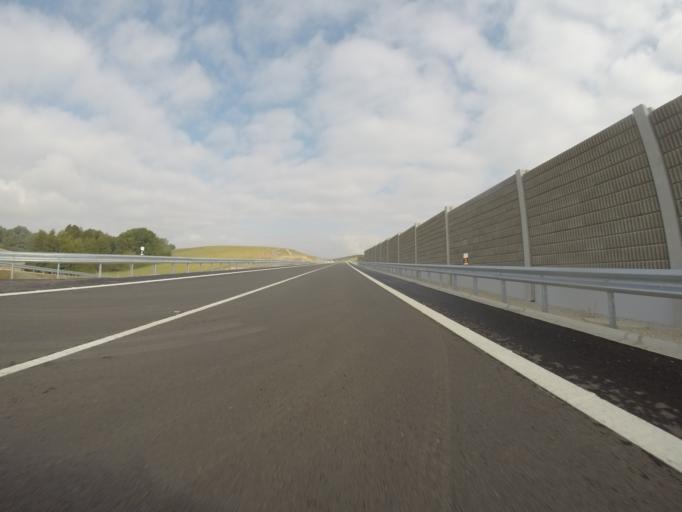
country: SK
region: Nitriansky
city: Banovce nad Bebravou
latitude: 48.7182
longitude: 18.2319
